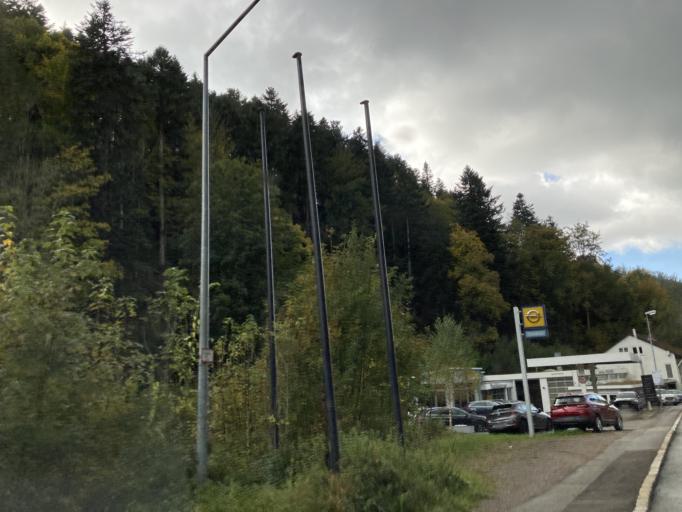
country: DE
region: Baden-Wuerttemberg
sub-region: Freiburg Region
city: Triberg im Schwarzwald
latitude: 48.1326
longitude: 8.2493
